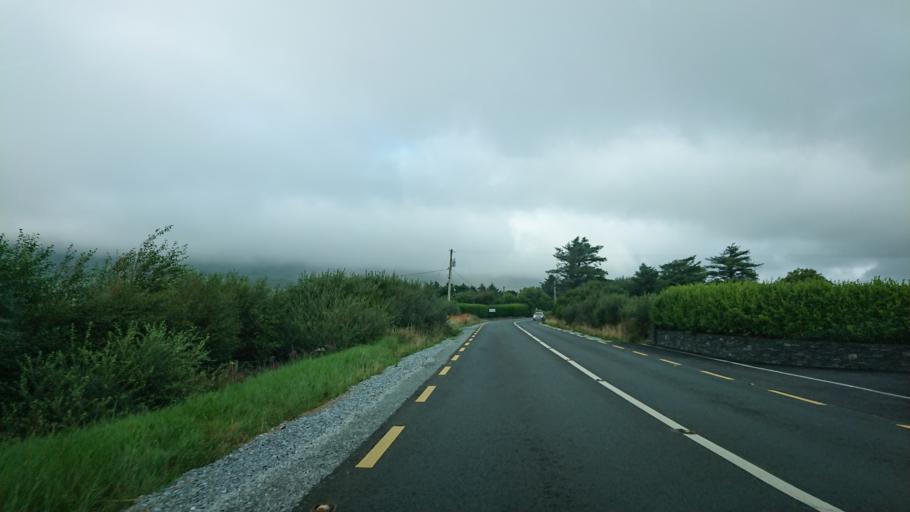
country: IE
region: Munster
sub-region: Ciarrai
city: Cahersiveen
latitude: 51.9558
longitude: -10.1942
